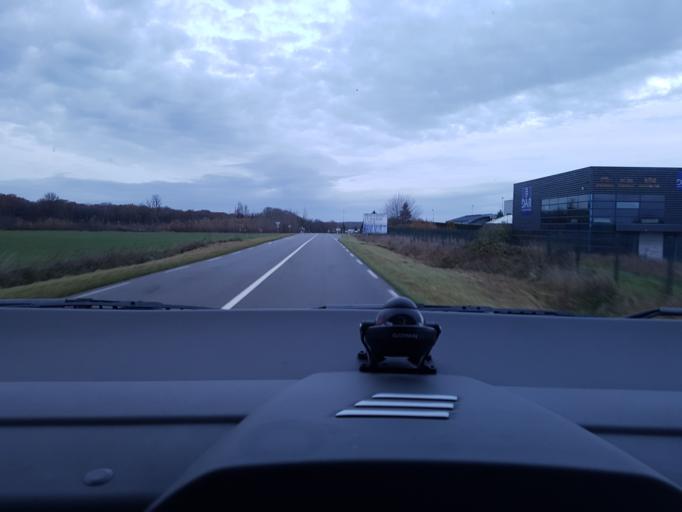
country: FR
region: Picardie
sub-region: Departement de la Somme
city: Poix-de-Picardie
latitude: 49.7634
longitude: 1.9722
